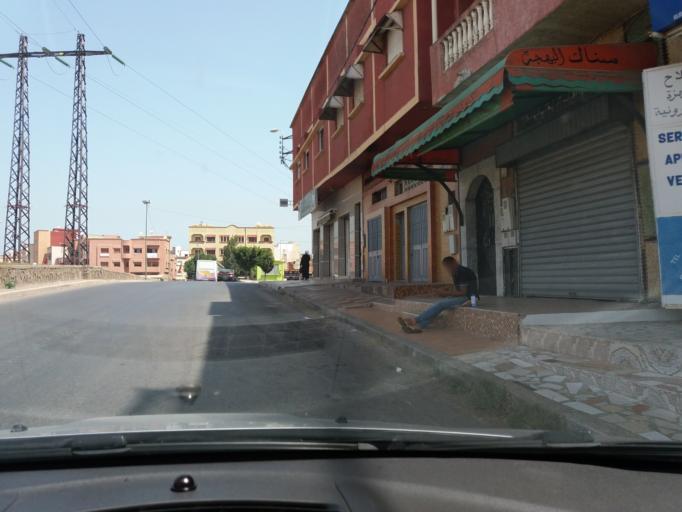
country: MA
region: Gharb-Chrarda-Beni Hssen
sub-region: Kenitra Province
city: Kenitra
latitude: 34.2648
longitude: -6.6168
